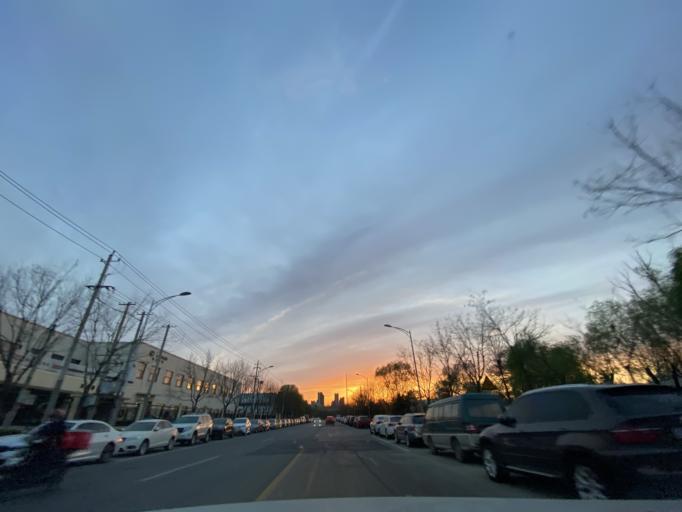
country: CN
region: Beijing
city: Qinghe
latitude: 40.0162
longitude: 116.3563
